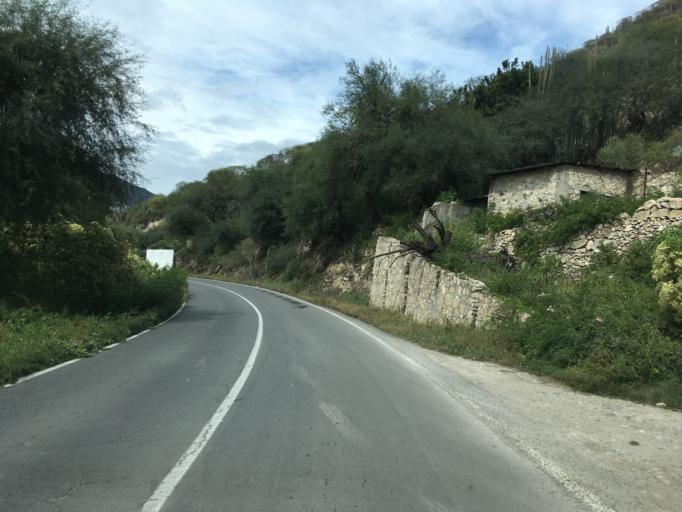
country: MX
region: Hidalgo
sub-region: San Agustin Metzquititlan
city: Mezquititlan
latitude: 20.5169
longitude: -98.7132
